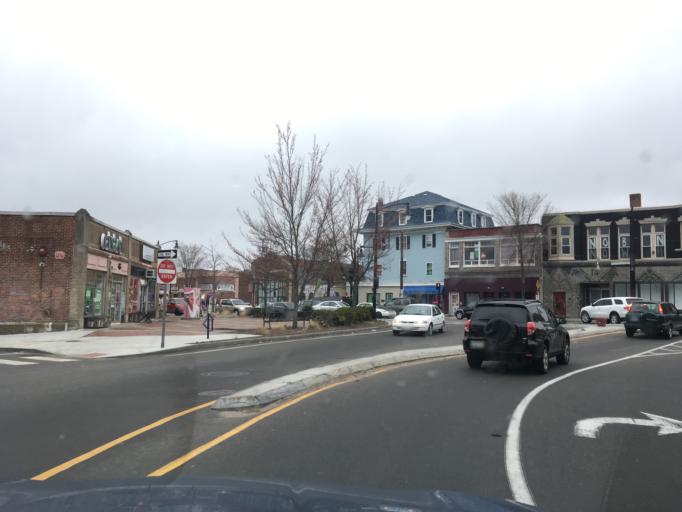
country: US
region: Rhode Island
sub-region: Providence County
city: Providence
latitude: 41.8171
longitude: -71.4436
